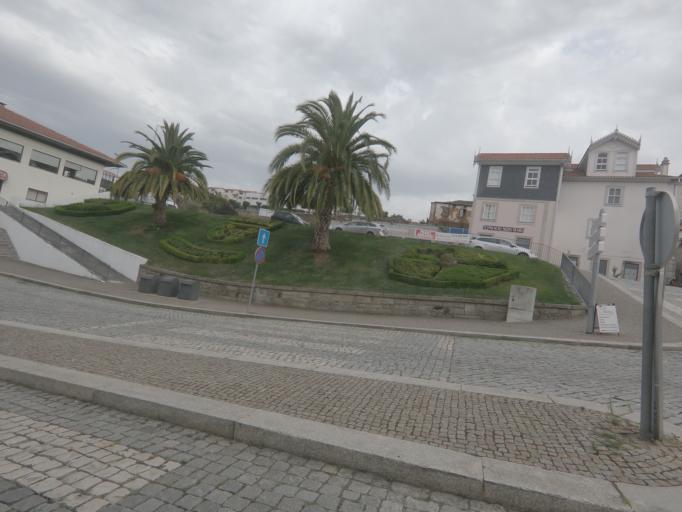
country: PT
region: Viseu
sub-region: Armamar
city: Armamar
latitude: 41.1094
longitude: -7.6922
